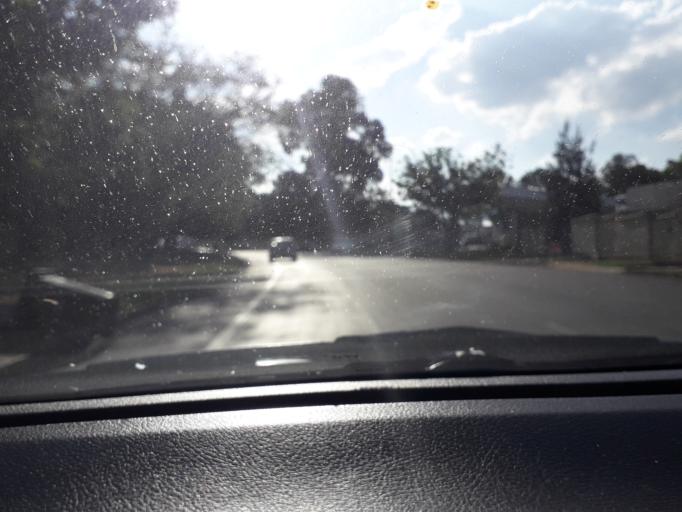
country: ZA
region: Gauteng
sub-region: City of Johannesburg Metropolitan Municipality
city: Modderfontein
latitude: -26.1254
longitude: 28.0886
